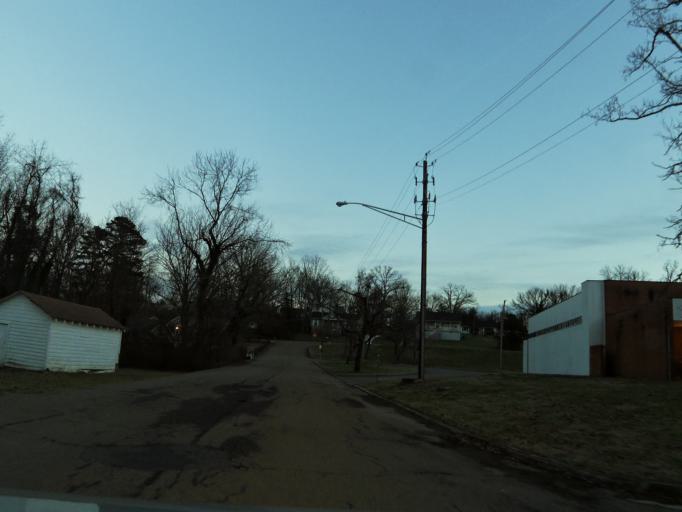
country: US
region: Tennessee
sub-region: Knox County
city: Knoxville
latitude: 35.9370
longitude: -83.9037
